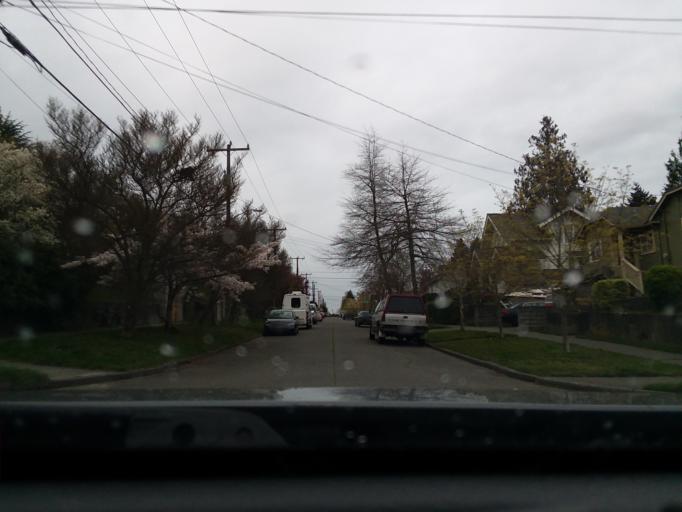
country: US
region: Washington
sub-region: King County
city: Shoreline
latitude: 47.6810
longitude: -122.3957
